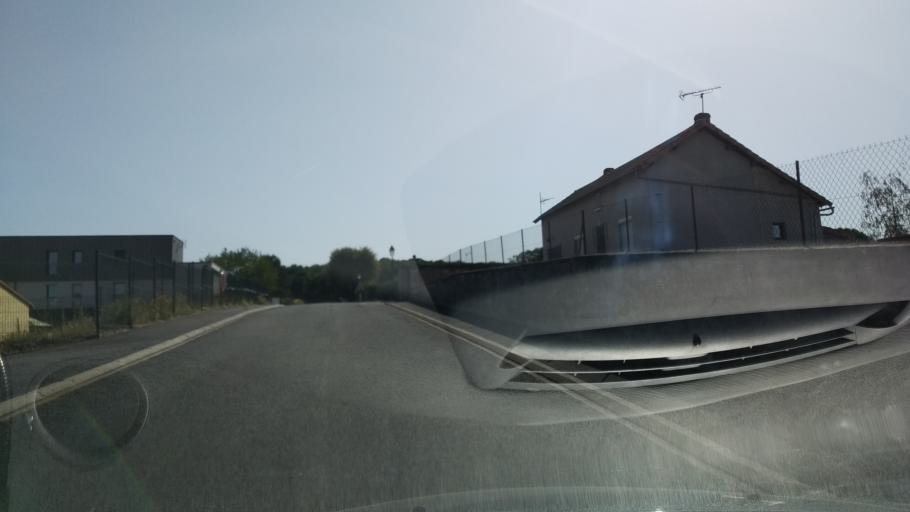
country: FR
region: Poitou-Charentes
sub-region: Departement de la Vienne
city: Lussac-les-Chateaux
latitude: 46.4439
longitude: 0.6598
